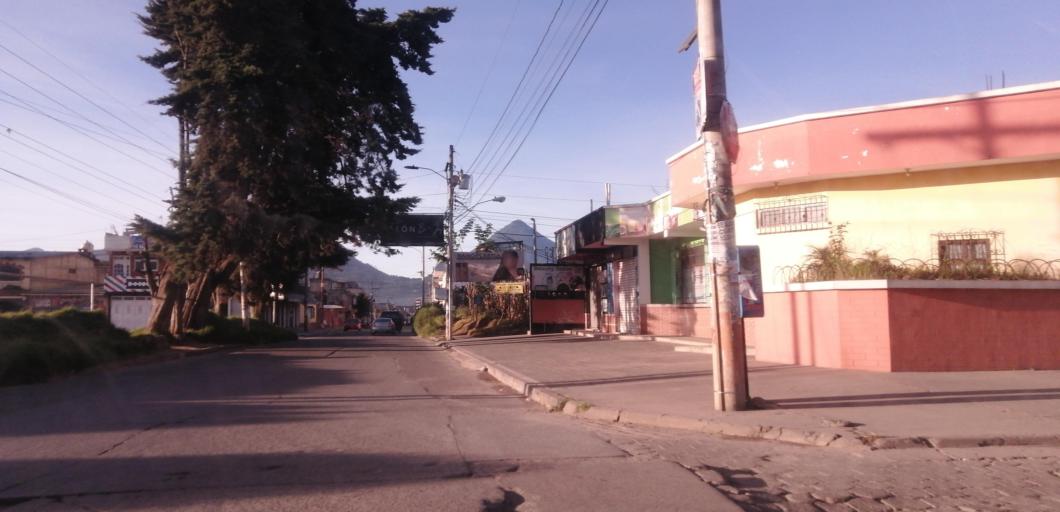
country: GT
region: Quetzaltenango
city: Olintepeque
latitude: 14.8664
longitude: -91.5211
